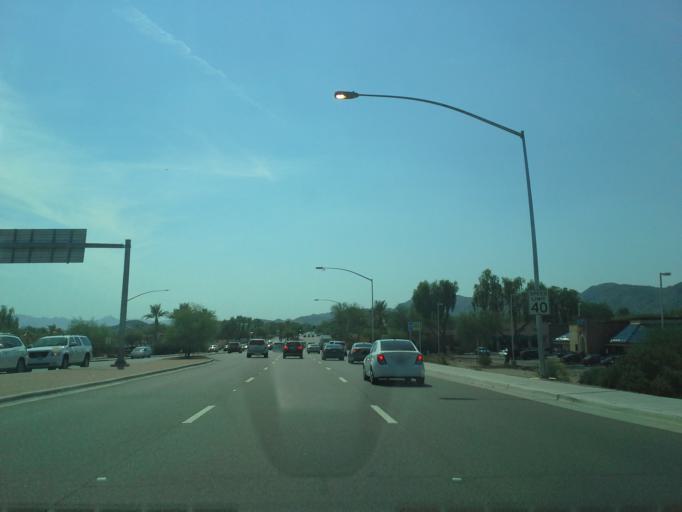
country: US
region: Arizona
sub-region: Maricopa County
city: Guadalupe
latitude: 33.3200
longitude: -111.9741
